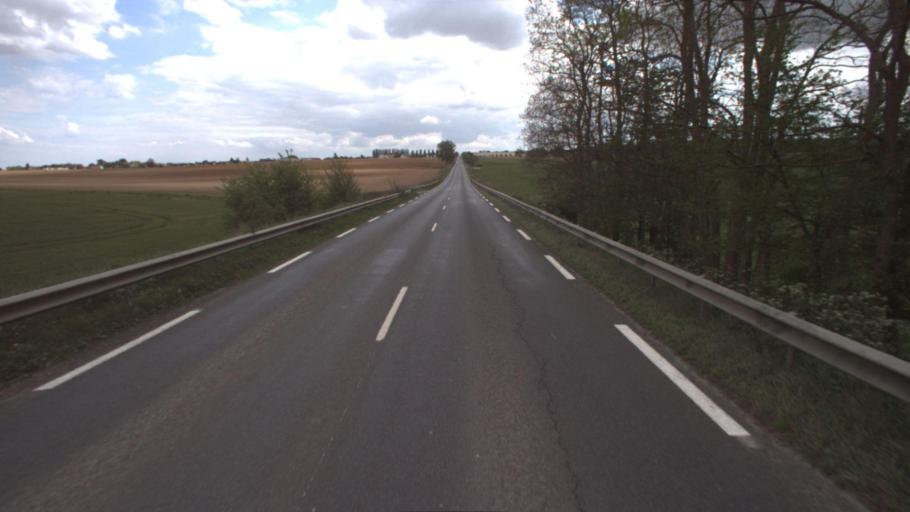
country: FR
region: Ile-de-France
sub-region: Departement de Seine-et-Marne
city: Saint-Soupplets
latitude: 49.0479
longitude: 2.7906
